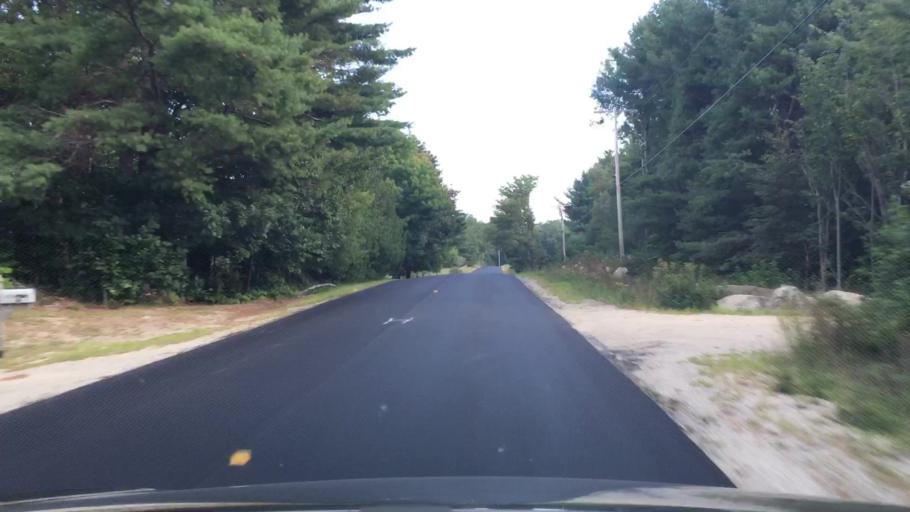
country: US
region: Maine
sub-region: Hancock County
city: Surry
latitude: 44.5288
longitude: -68.6117
